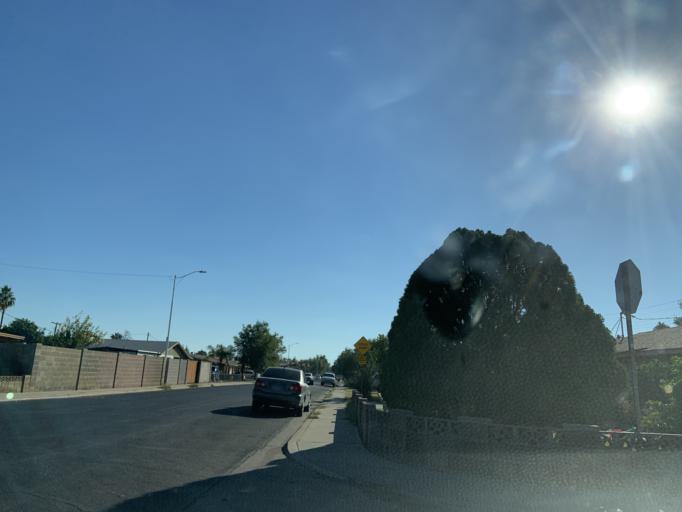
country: US
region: Arizona
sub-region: Maricopa County
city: Tempe
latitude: 33.4029
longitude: -111.8698
